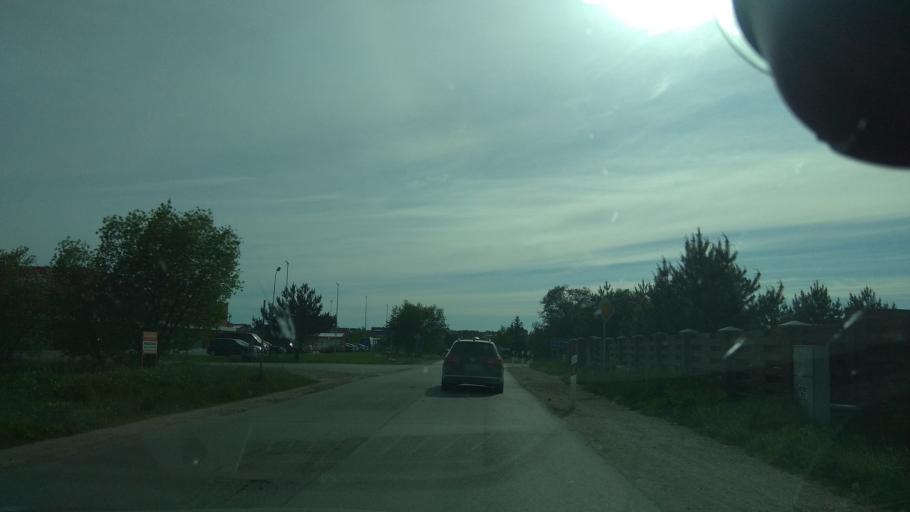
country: LT
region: Klaipedos apskritis
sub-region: Klaipeda
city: Klaipeda
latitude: 55.7532
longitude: 21.1762
